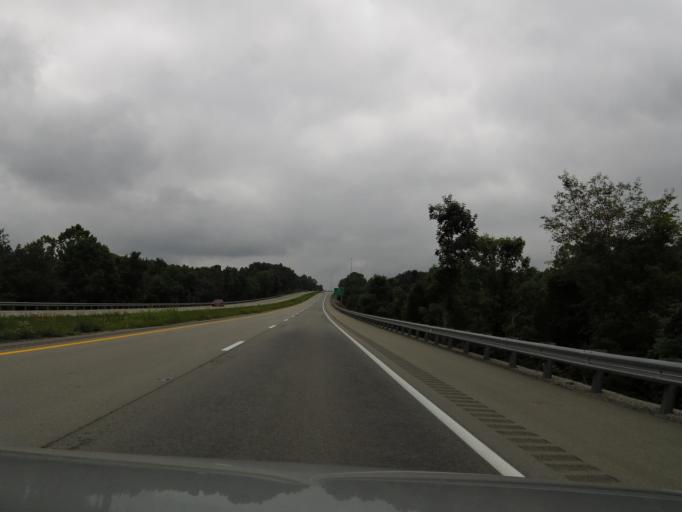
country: US
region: Kentucky
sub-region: Grayson County
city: Leitchfield
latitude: 37.4128
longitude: -86.5159
